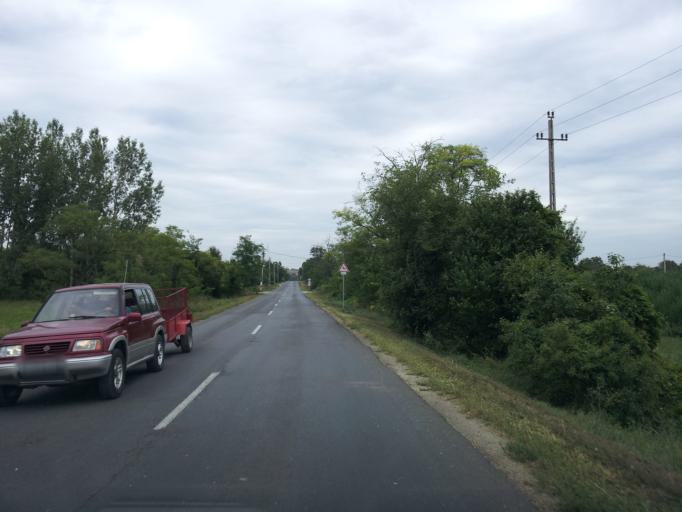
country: HU
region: Pest
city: Tarnok
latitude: 47.3773
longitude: 18.8563
